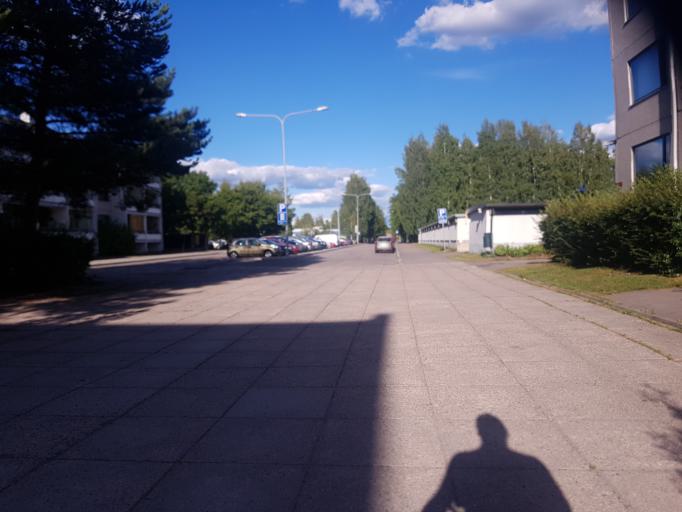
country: FI
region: Uusimaa
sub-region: Helsinki
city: Vantaa
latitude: 60.2738
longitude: 24.9857
